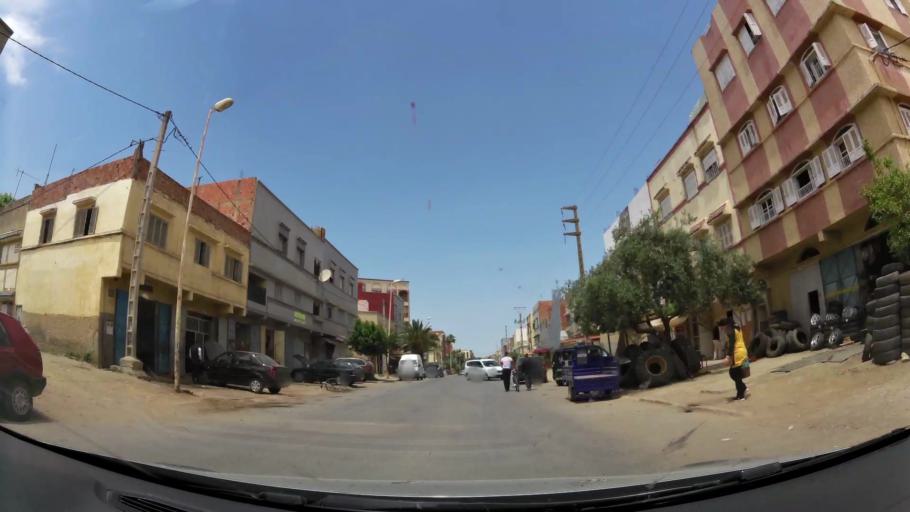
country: MA
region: Rabat-Sale-Zemmour-Zaer
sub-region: Khemisset
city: Khemisset
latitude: 33.8229
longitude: -6.0770
